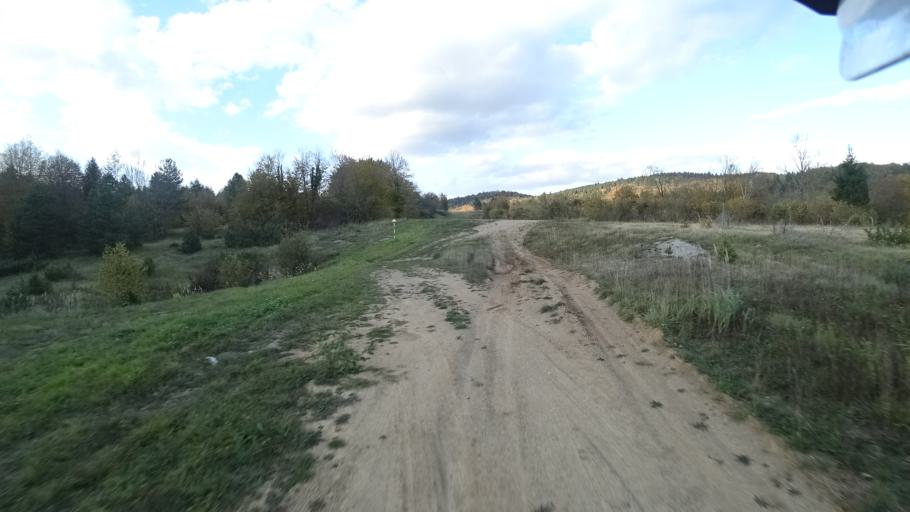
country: HR
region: Karlovacka
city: Plaski
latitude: 45.0025
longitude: 15.4256
